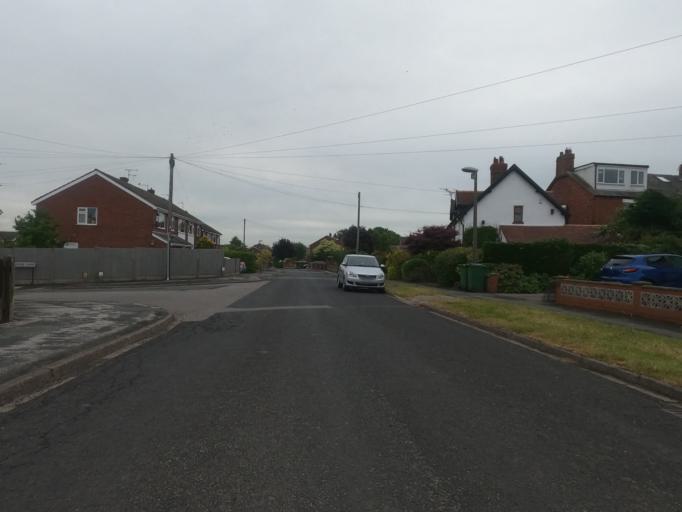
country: GB
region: England
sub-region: Cheshire West and Chester
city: Winsford
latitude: 53.2204
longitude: -2.5144
